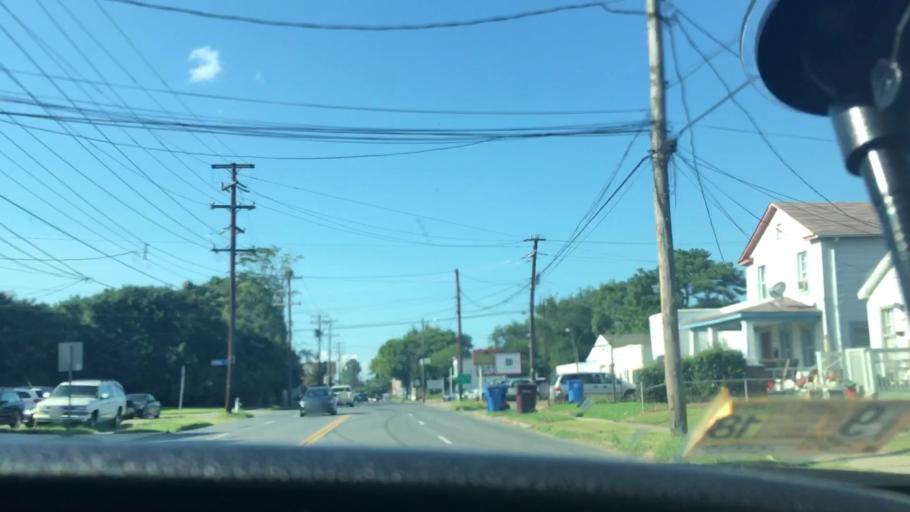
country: US
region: Virginia
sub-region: City of Chesapeake
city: Chesapeake
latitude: 36.8115
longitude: -76.2779
